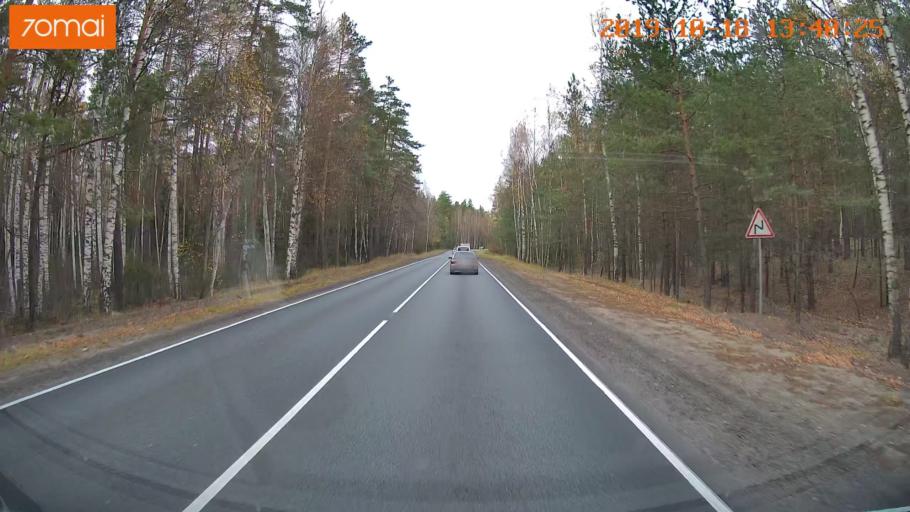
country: RU
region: Rjazan
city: Solotcha
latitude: 54.9094
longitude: 39.9985
